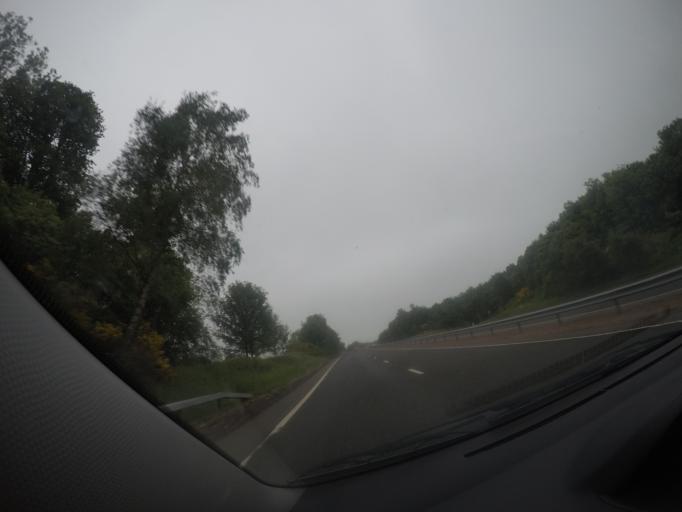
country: GB
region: Scotland
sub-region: Angus
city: Forfar
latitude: 56.5979
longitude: -2.9092
